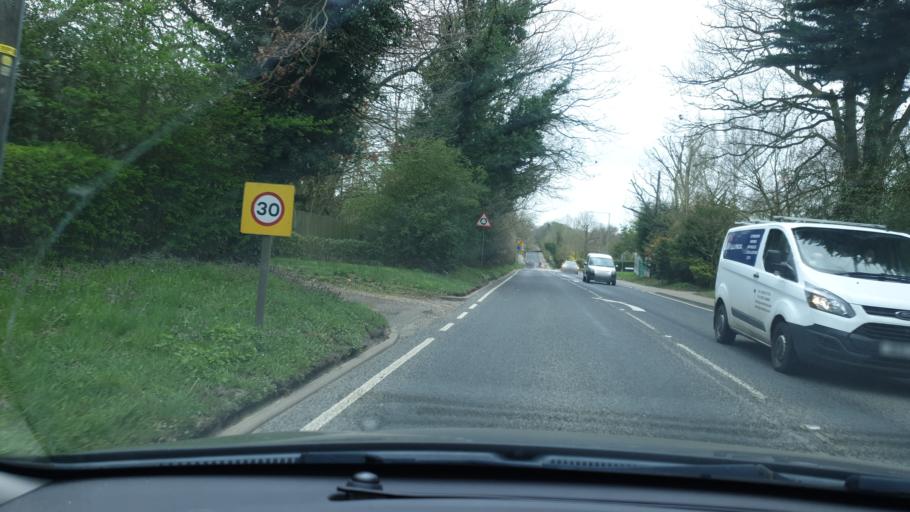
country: GB
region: England
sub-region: Essex
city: Great Horkesley
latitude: 51.9254
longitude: 0.8817
